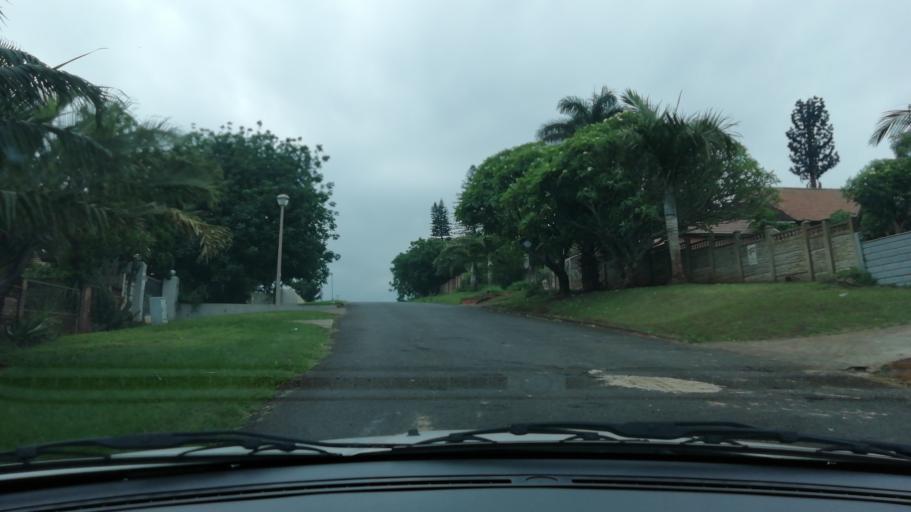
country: ZA
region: KwaZulu-Natal
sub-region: uThungulu District Municipality
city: Empangeni
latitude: -28.7384
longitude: 31.8996
